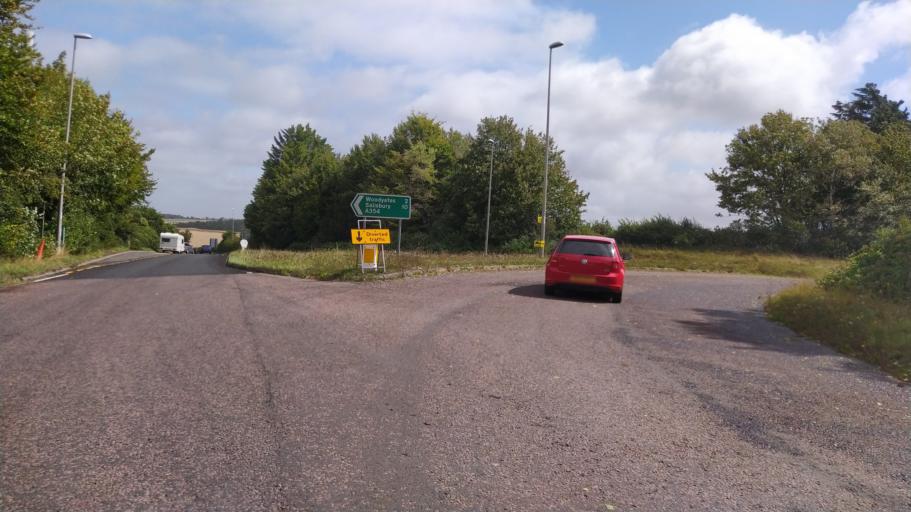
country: GB
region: England
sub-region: Wiltshire
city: Bower Chalke
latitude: 50.9493
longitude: -1.9856
